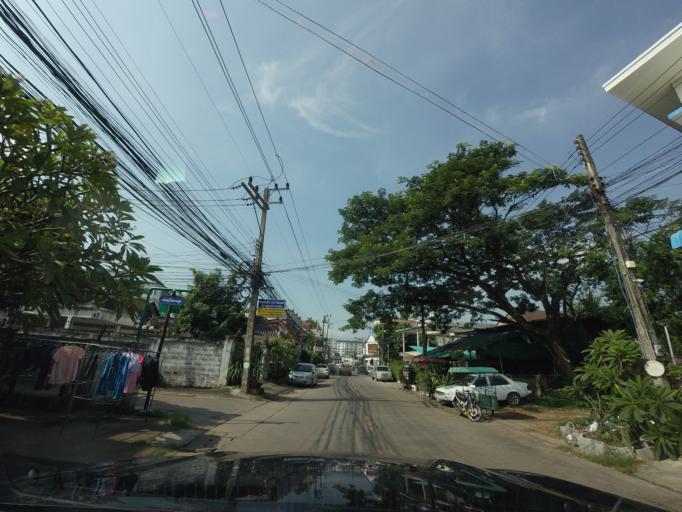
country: TH
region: Khon Kaen
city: Khon Kaen
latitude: 16.4301
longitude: 102.8551
